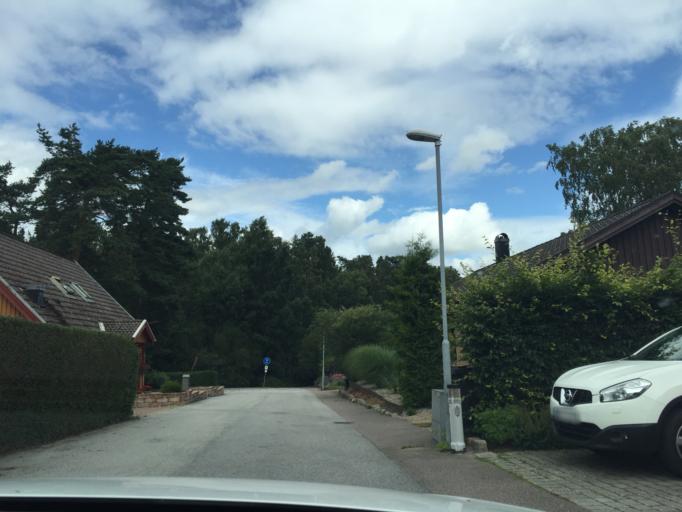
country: SE
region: Skane
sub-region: Sjobo Kommun
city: Blentarp
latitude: 55.5828
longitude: 13.5943
